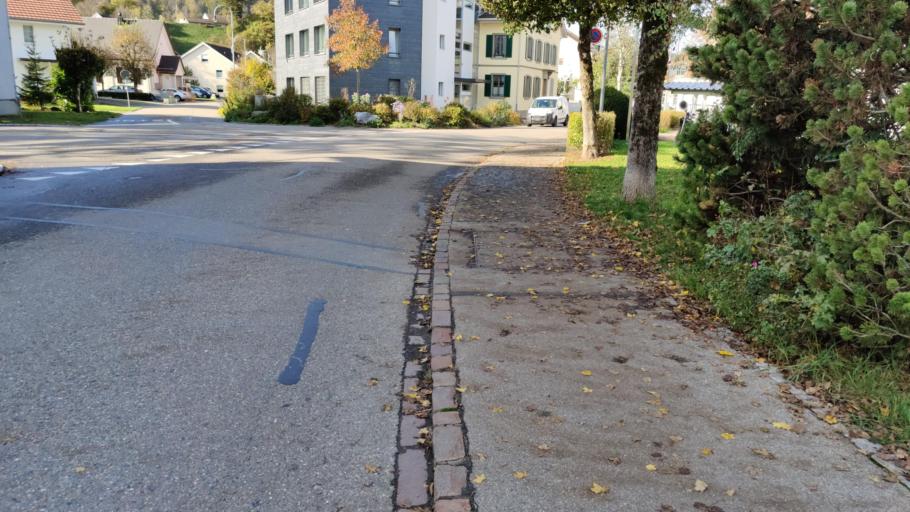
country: CH
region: Zurich
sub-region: Bezirk Pfaeffikon
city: Wila
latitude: 47.4173
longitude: 8.8490
